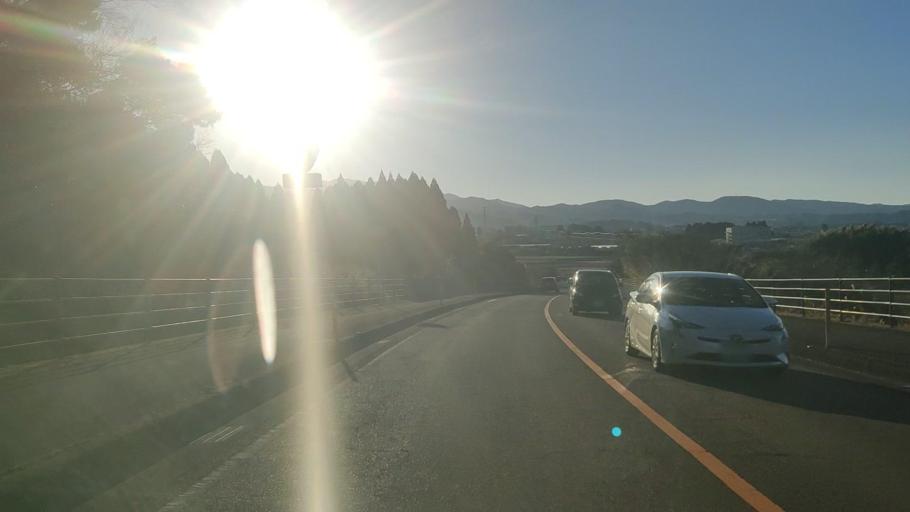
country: JP
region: Miyazaki
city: Miyazaki-shi
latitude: 31.8315
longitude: 131.3166
